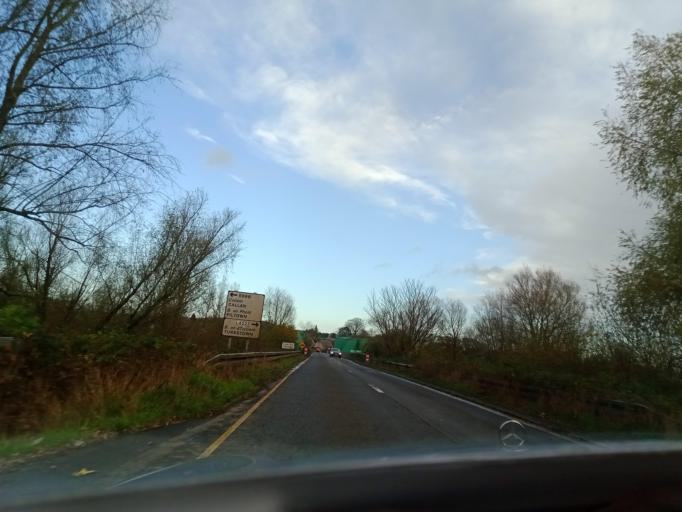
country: IE
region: Leinster
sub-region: Kilkenny
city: Piltown
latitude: 52.3266
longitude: -7.3180
